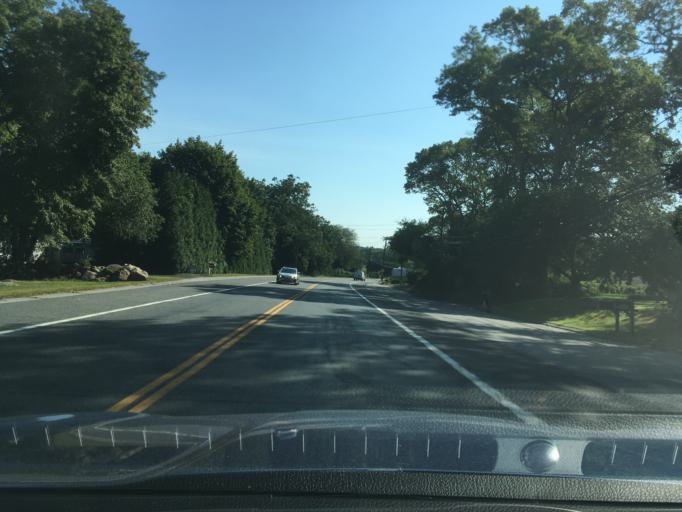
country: US
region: Rhode Island
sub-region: Washington County
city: Exeter
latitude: 41.5769
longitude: -71.5324
